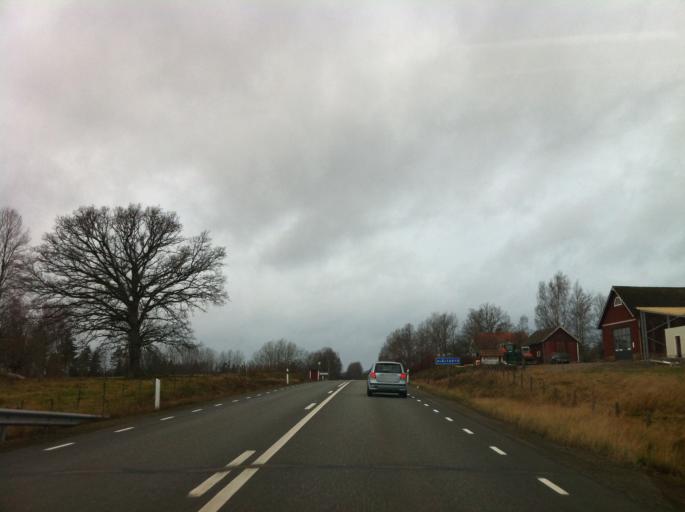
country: SE
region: Joenkoeping
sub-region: Vetlanda Kommun
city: Landsbro
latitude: 57.4035
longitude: 14.9456
